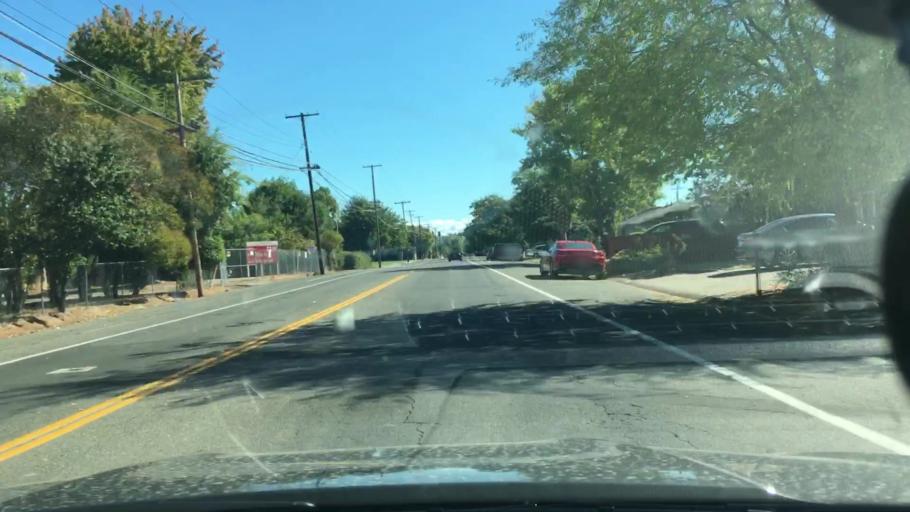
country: US
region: California
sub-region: Sacramento County
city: Arden-Arcade
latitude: 38.5886
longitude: -121.3912
